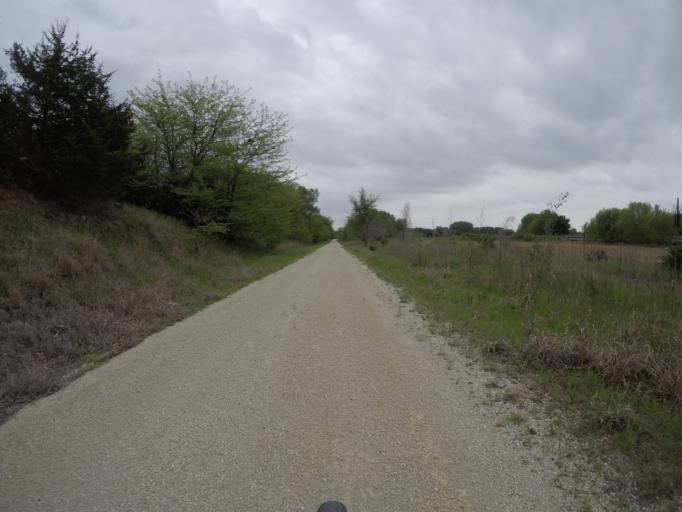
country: US
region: Nebraska
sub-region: Gage County
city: Wymore
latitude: 40.1113
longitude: -96.6234
